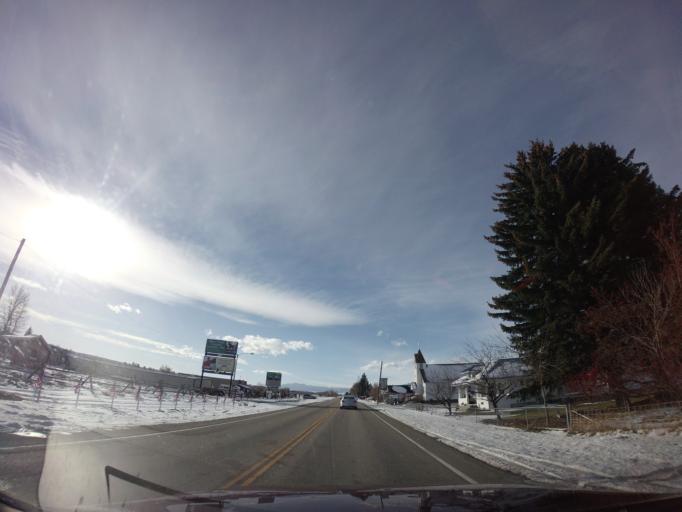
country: US
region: Montana
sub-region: Carbon County
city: Red Lodge
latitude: 45.3573
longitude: -109.1696
